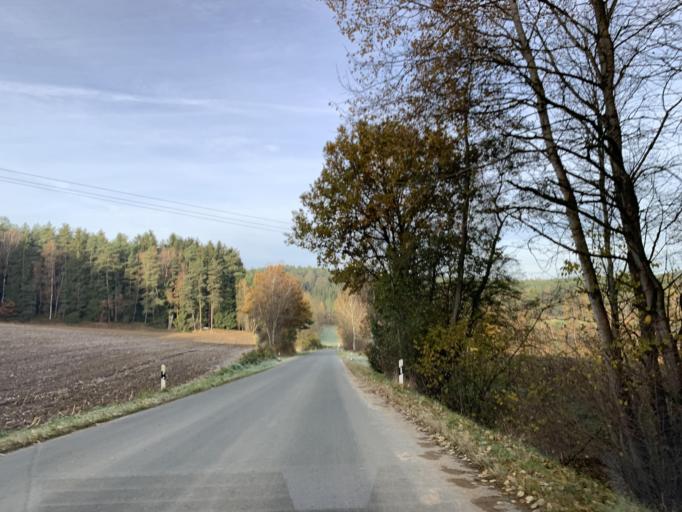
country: DE
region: Bavaria
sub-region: Upper Palatinate
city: Thanstein
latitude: 49.3449
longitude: 12.4380
